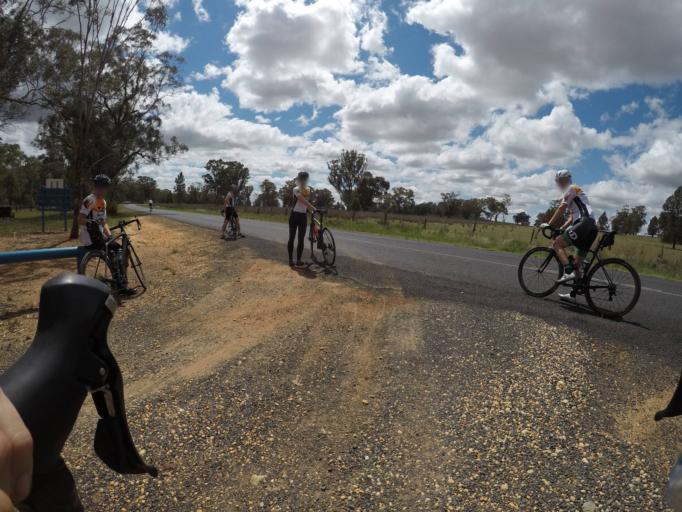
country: AU
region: New South Wales
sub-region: Dubbo Municipality
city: Dubbo
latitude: -32.4881
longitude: 148.5558
